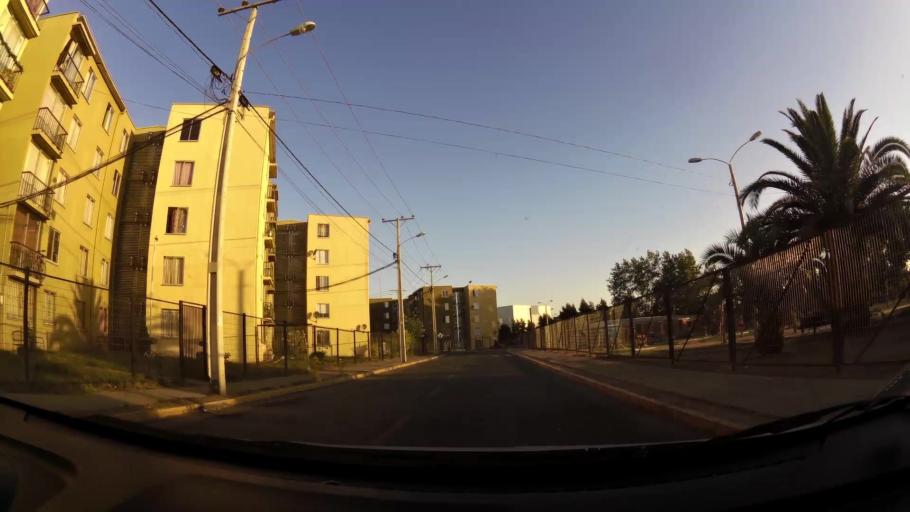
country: CL
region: Maule
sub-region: Provincia de Talca
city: Talca
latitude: -35.4431
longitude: -71.6407
